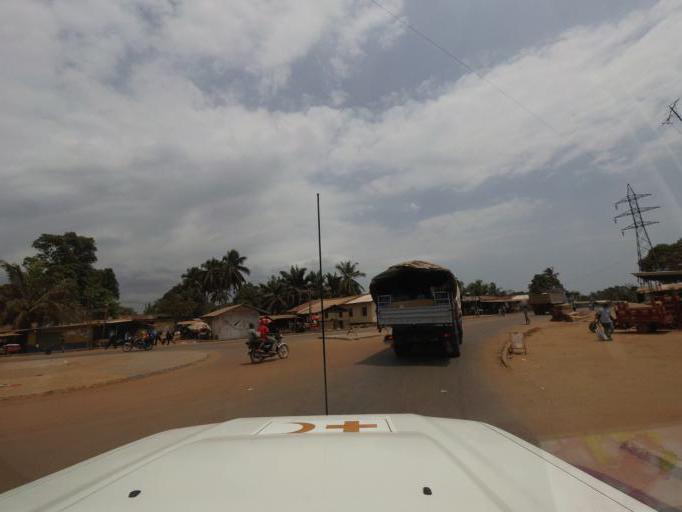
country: LR
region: Montserrado
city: Monrovia
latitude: 6.3055
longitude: -10.6907
